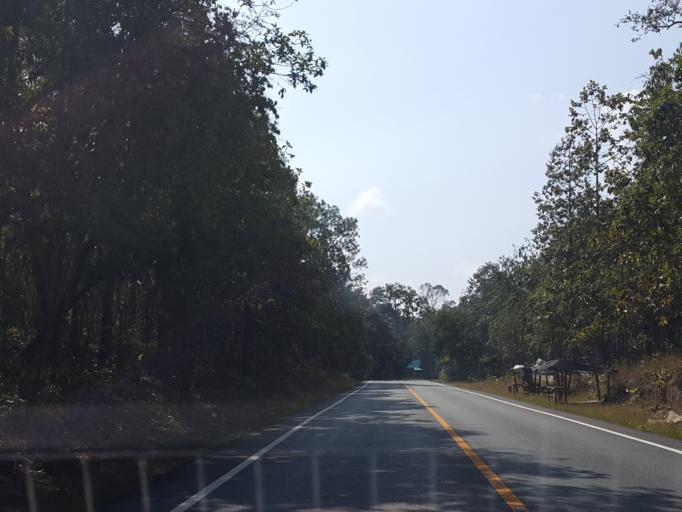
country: TH
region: Chiang Mai
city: Hot
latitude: 18.1543
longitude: 98.4293
